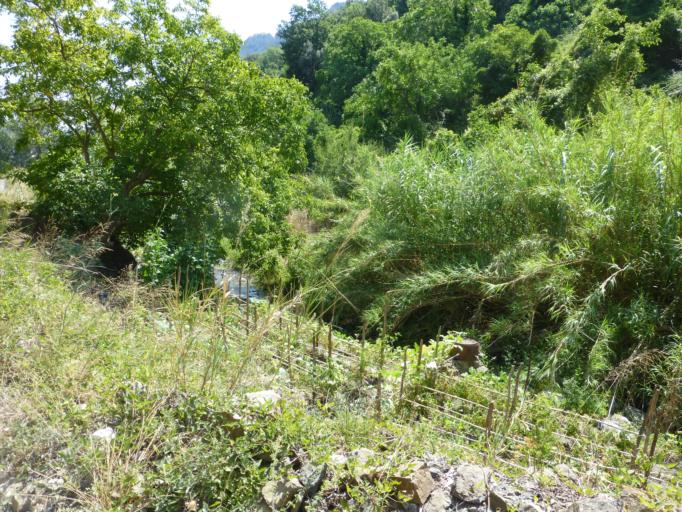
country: IT
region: Calabria
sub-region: Provincia di Reggio Calabria
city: Pazzano
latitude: 38.4771
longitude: 16.4429
